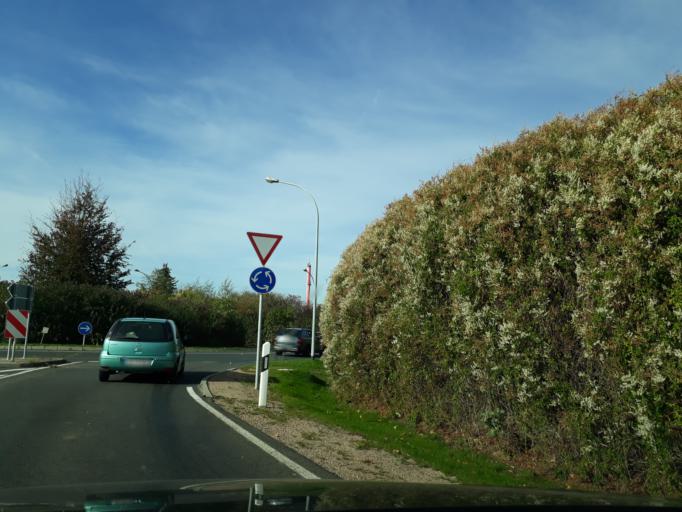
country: DE
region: Saxony
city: Mochau
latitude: 51.1209
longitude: 13.1481
